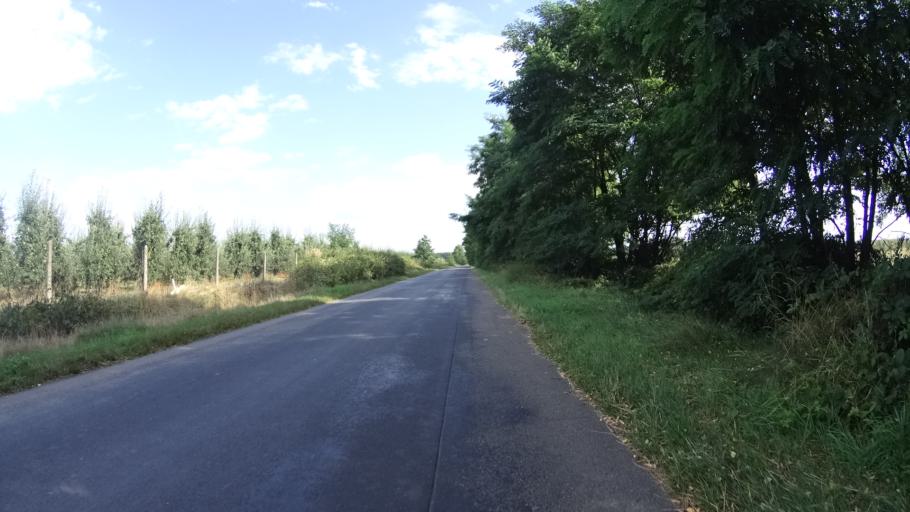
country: PL
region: Masovian Voivodeship
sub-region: Powiat grojecki
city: Mogielnica
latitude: 51.6844
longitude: 20.7579
